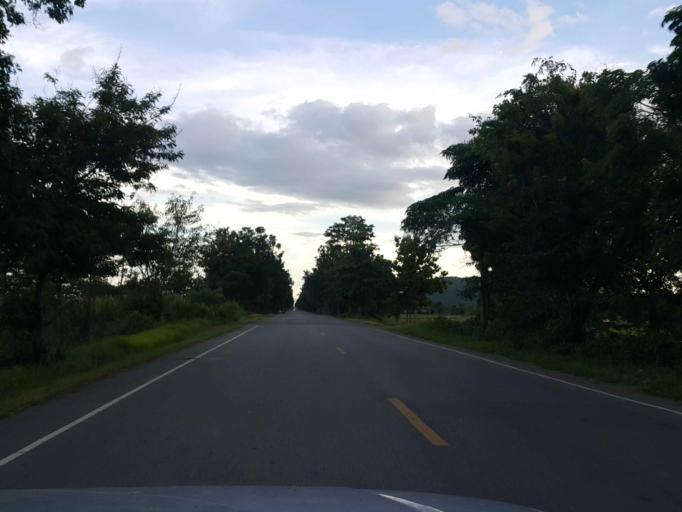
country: TH
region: Sukhothai
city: Sawankhalok
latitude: 17.3223
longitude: 99.7370
